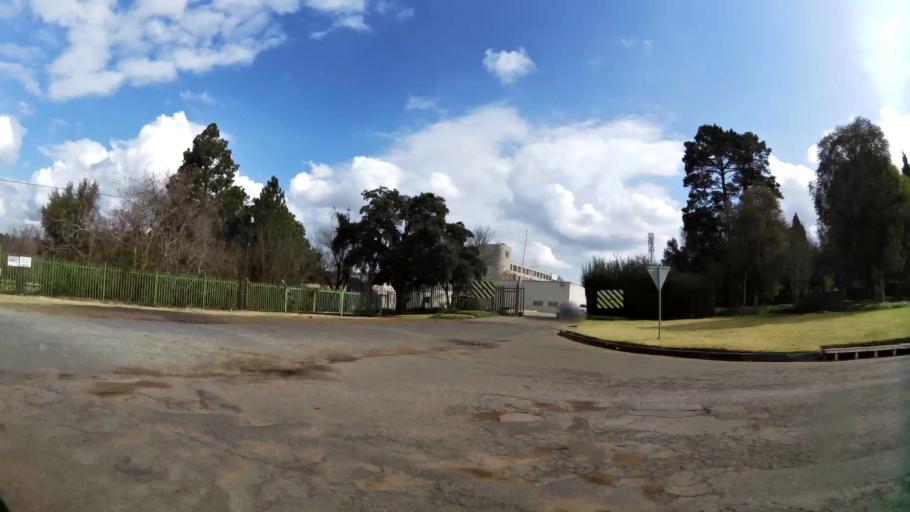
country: ZA
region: Gauteng
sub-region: Sedibeng District Municipality
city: Vanderbijlpark
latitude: -26.7485
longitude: 27.8295
